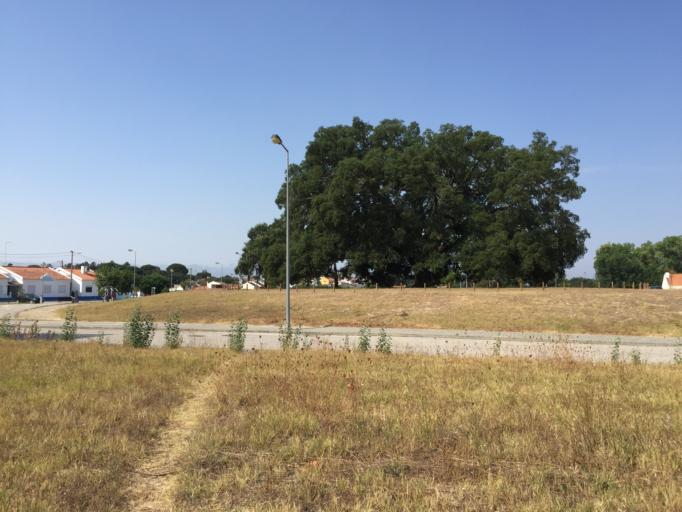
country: PT
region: Setubal
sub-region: Setubal
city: Setubal
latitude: 38.5868
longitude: -8.6904
